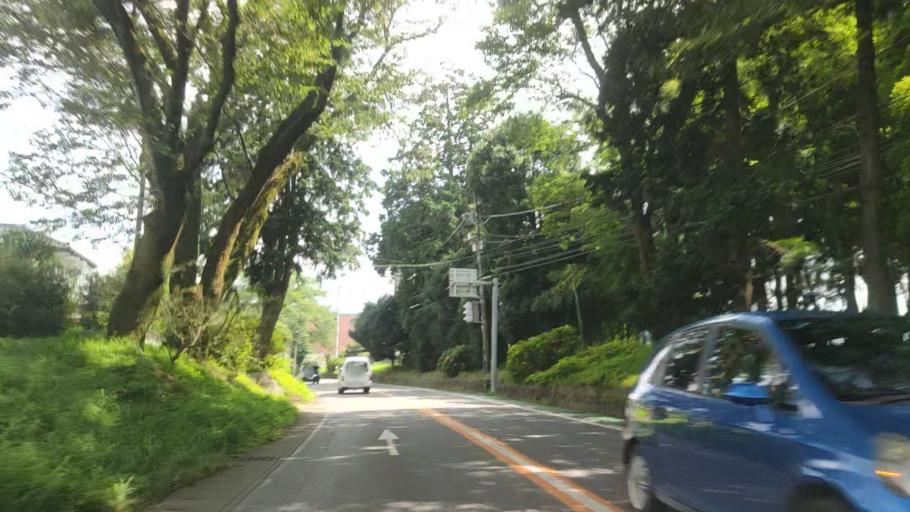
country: JP
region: Tochigi
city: Utsunomiya-shi
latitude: 36.6128
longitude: 139.8544
